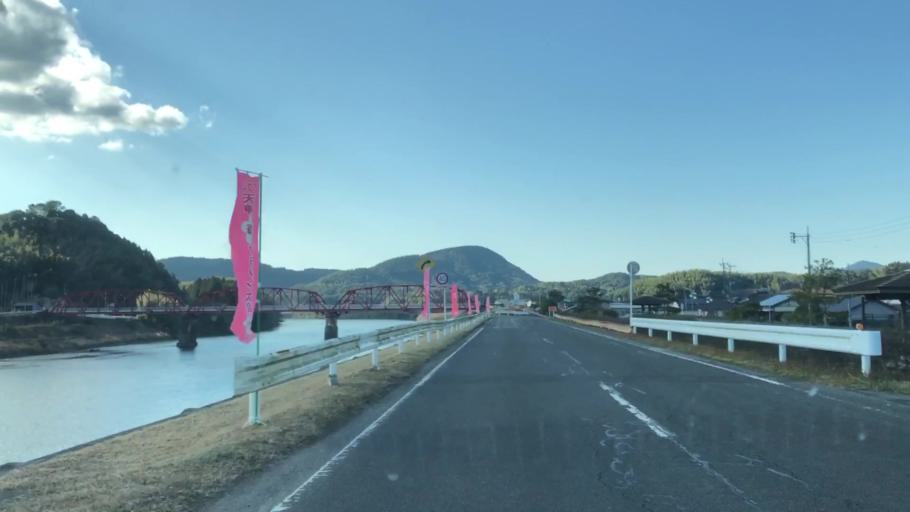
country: JP
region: Kagoshima
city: Satsumasendai
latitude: 31.8615
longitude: 130.3397
